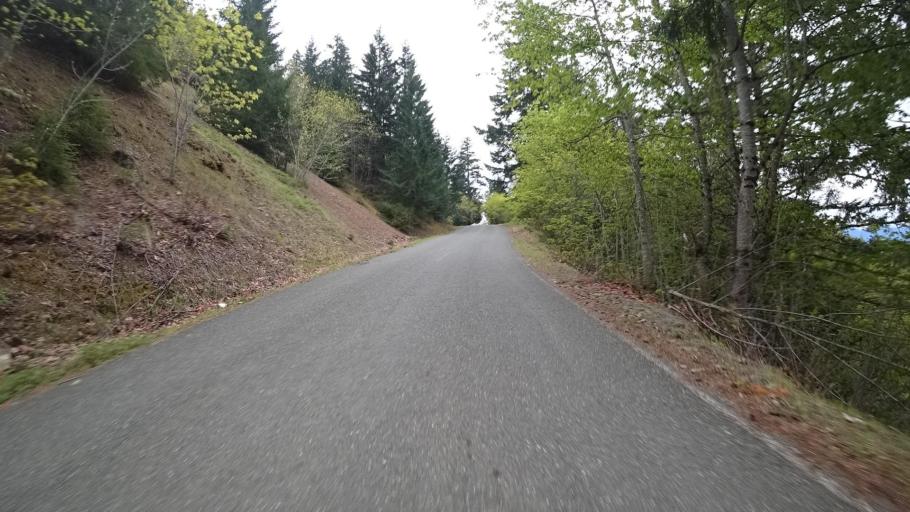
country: US
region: California
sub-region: Humboldt County
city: Redway
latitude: 40.1578
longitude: -123.5571
